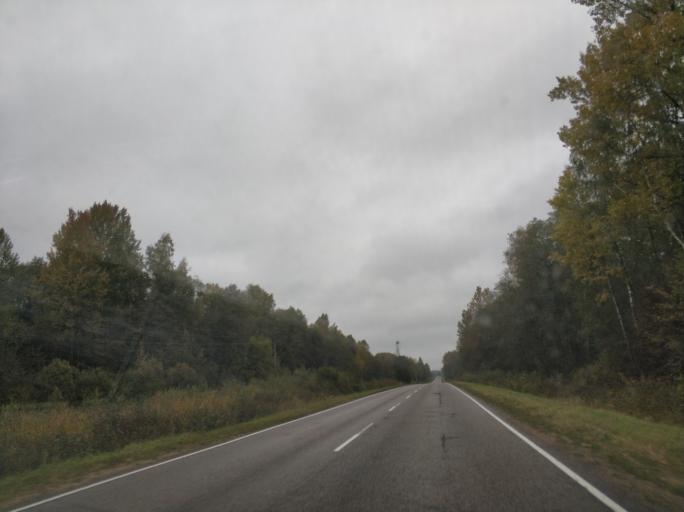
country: BY
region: Vitebsk
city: Rasony
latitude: 56.0804
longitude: 28.7166
